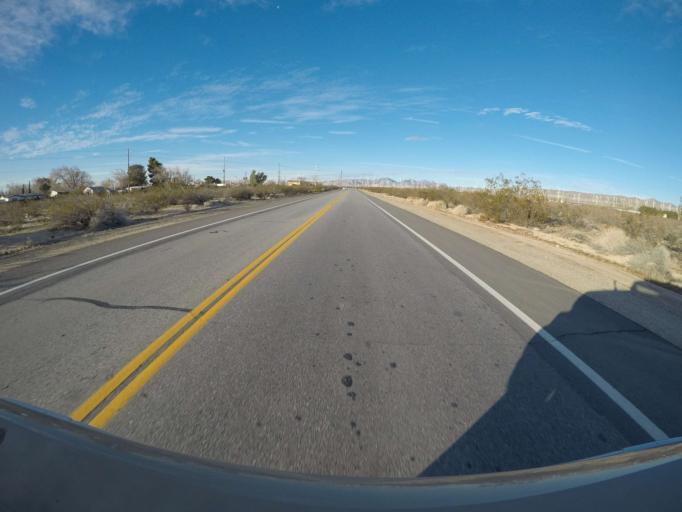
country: US
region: California
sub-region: Kern County
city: Mojave
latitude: 35.0546
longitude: -118.1903
